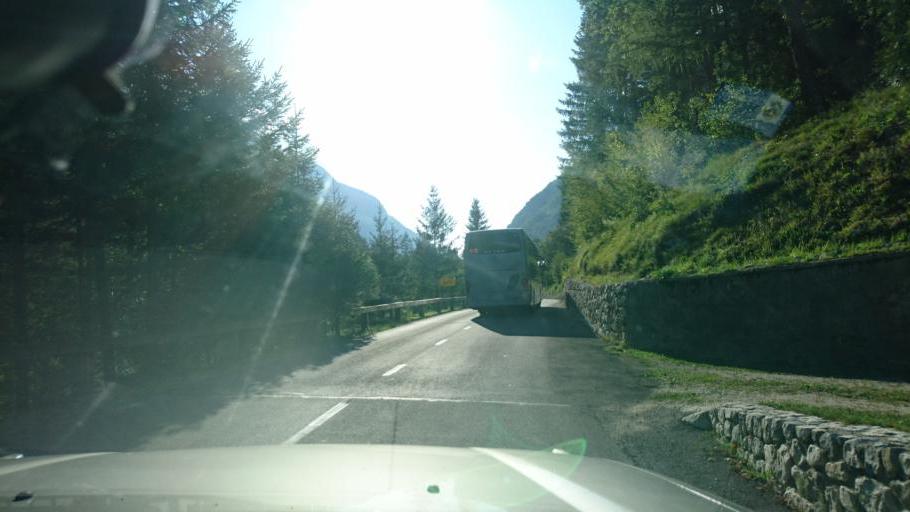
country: SI
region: Bovec
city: Bovec
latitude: 46.3406
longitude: 13.6586
